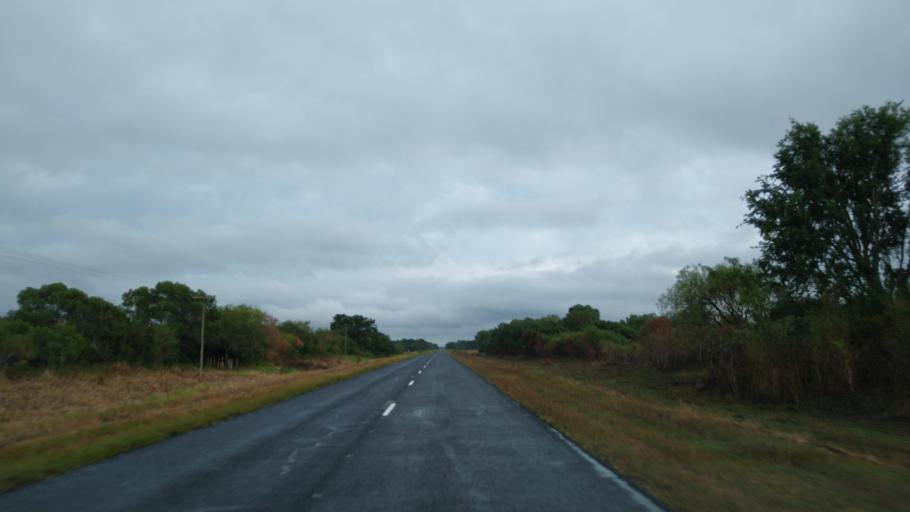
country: AR
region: Corrientes
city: Loreto
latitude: -27.7464
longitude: -57.2527
